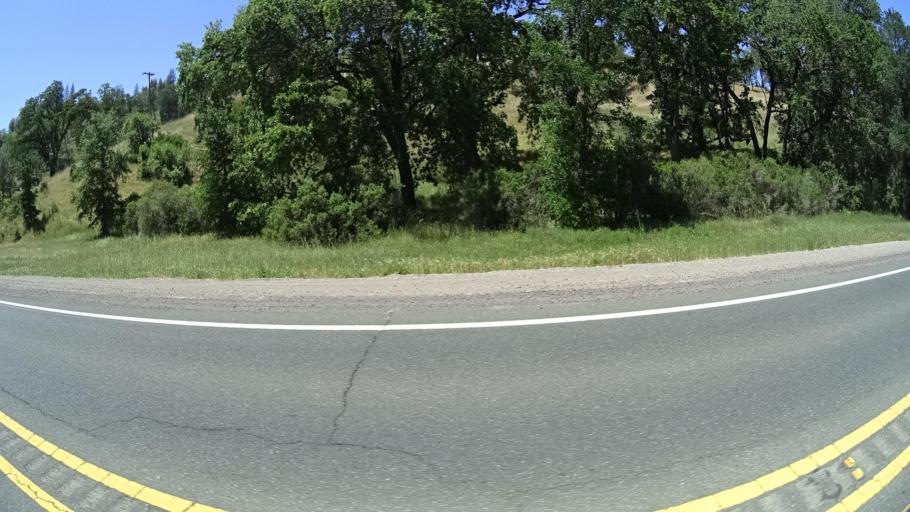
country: US
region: California
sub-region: Lake County
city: Lower Lake
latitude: 38.8684
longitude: -122.6228
